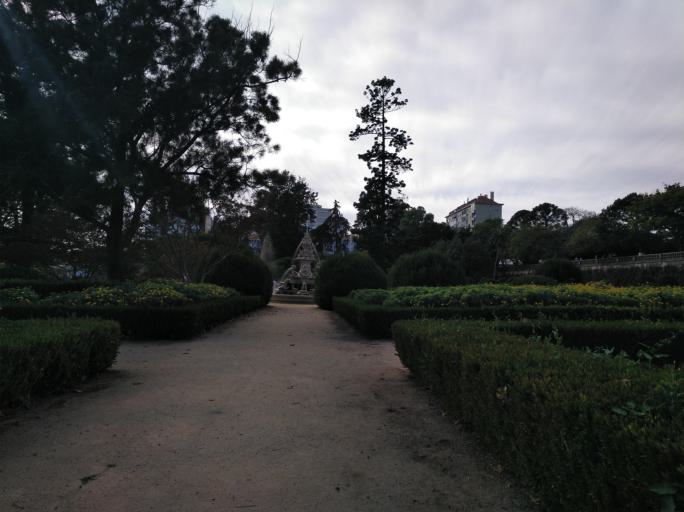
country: PT
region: Lisbon
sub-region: Oeiras
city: Alges
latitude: 38.7062
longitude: -9.2003
